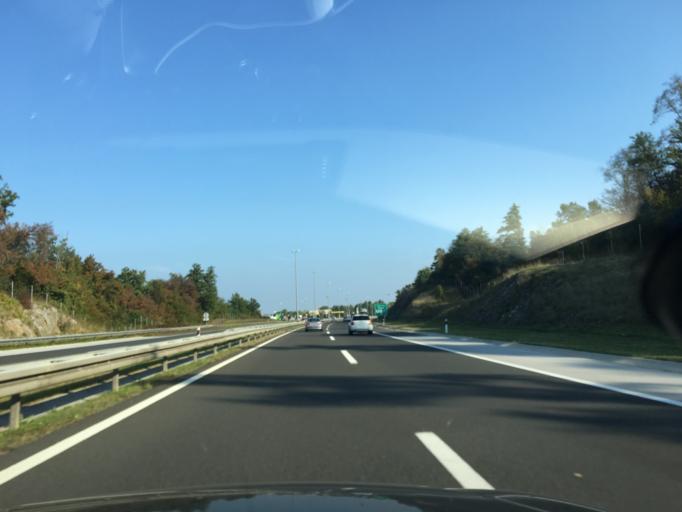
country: HR
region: Karlovacka
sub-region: Grad Ogulin
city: Ogulin
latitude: 45.3042
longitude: 15.2789
